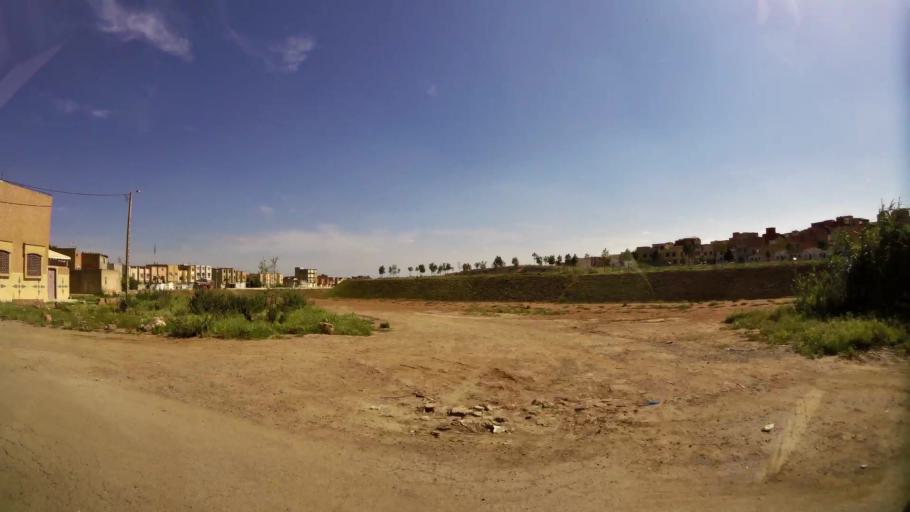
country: MA
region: Oriental
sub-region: Oujda-Angad
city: Oujda
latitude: 34.6548
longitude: -1.9329
